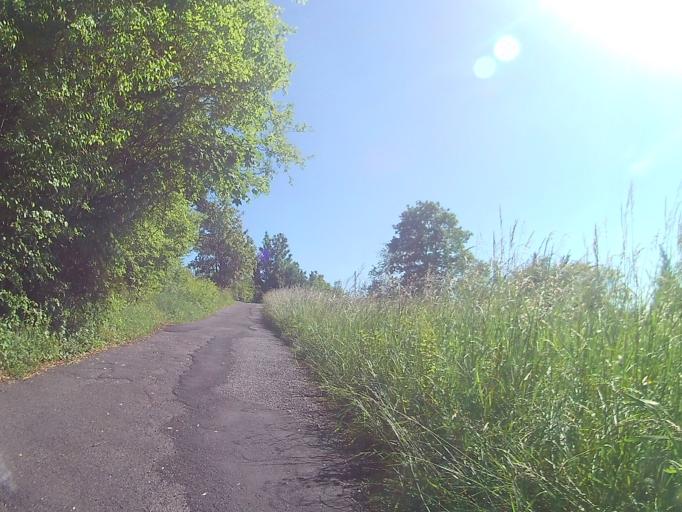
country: DE
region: Baden-Wuerttemberg
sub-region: Regierungsbezirk Stuttgart
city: Fellbach
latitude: 48.7706
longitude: 9.2775
